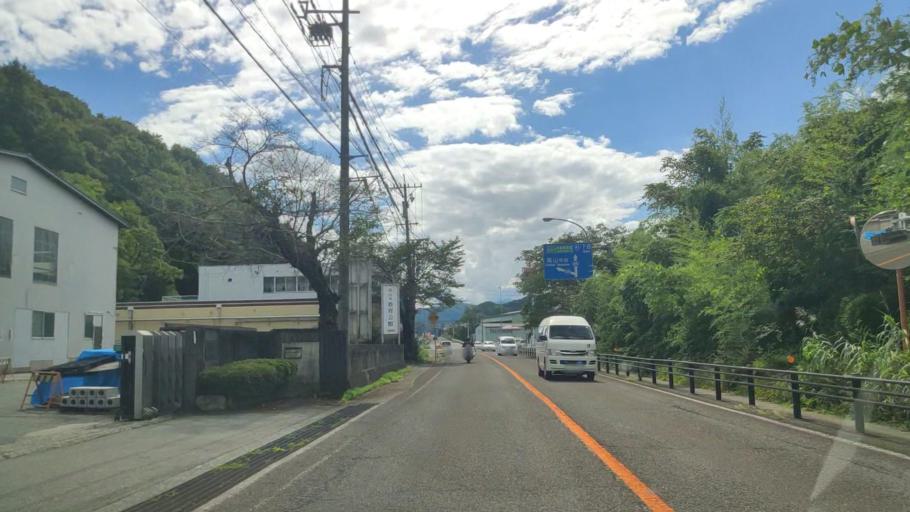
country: JP
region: Gifu
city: Takayama
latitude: 36.1712
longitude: 137.2466
